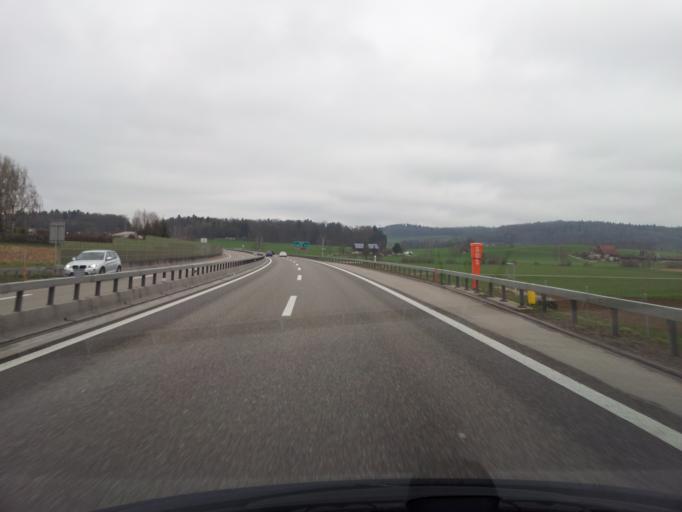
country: CH
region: Zurich
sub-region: Bezirk Andelfingen
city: Kleinandelfingen
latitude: 47.6221
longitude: 8.6820
